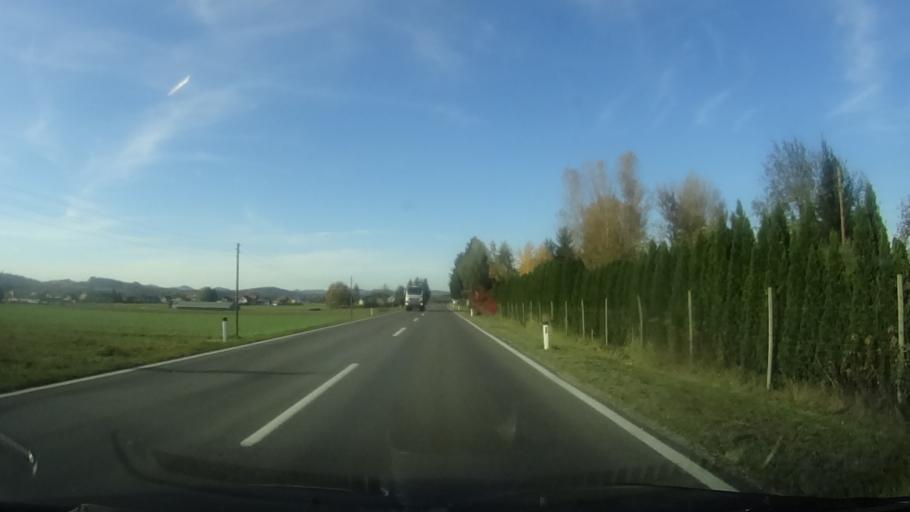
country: AT
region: Styria
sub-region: Politischer Bezirk Leibnitz
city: Kaindorf an der Sulm
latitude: 46.8098
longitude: 15.5284
